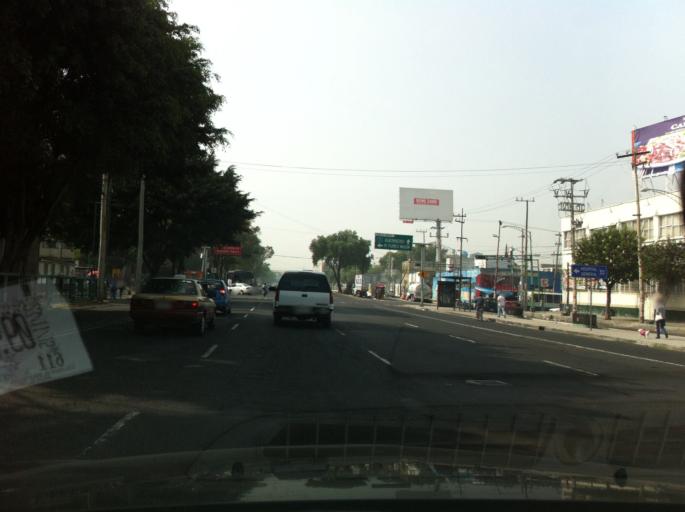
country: MX
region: Mexico City
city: Cuauhtemoc
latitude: 19.4554
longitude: -99.1396
